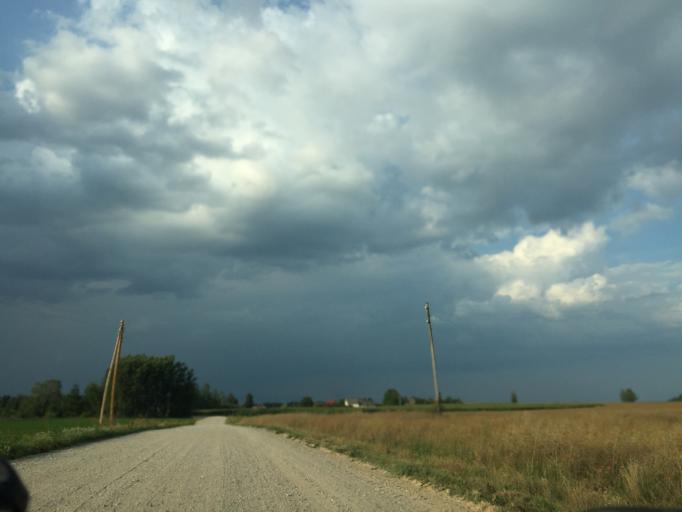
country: LV
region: Dobeles Rajons
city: Dobele
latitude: 56.5930
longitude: 23.3107
